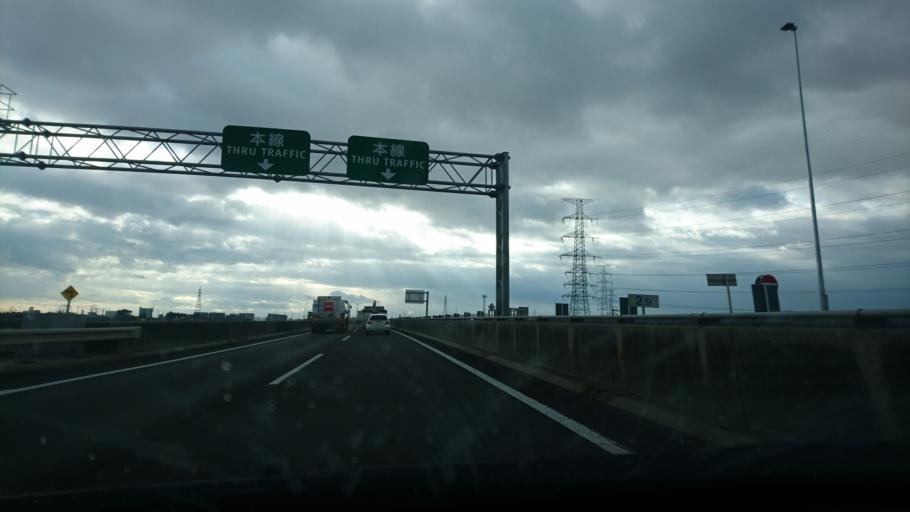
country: JP
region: Miyagi
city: Rifu
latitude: 38.3032
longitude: 140.9806
